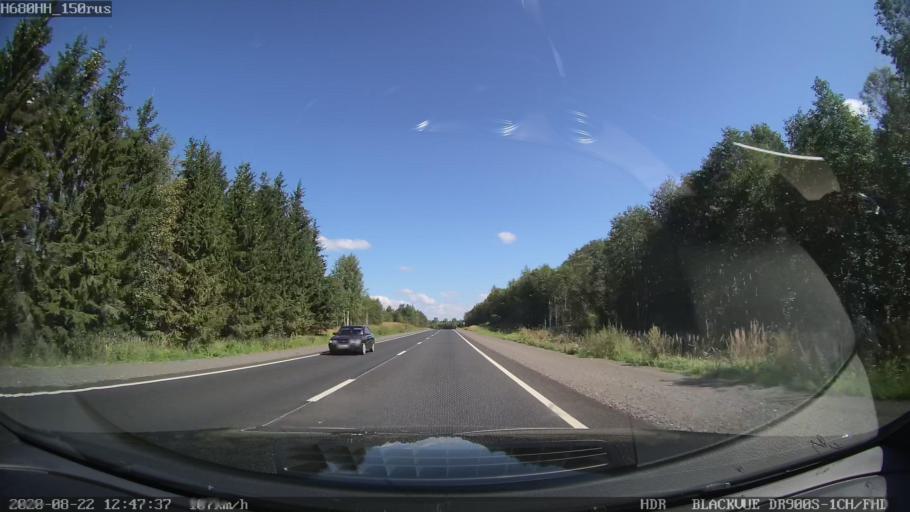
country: RU
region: Tverskaya
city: Rameshki
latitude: 57.4307
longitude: 36.1709
